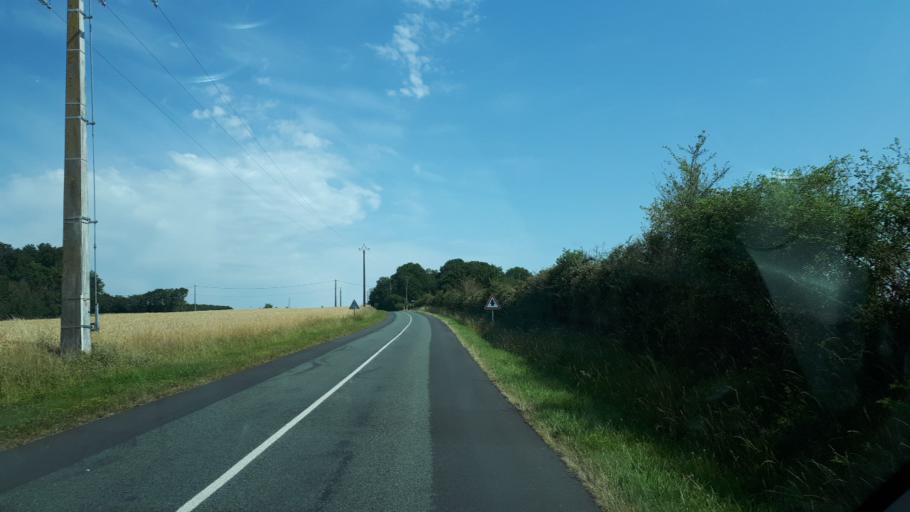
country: FR
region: Centre
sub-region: Departement du Loir-et-Cher
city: Aze
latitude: 47.8597
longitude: 1.0041
